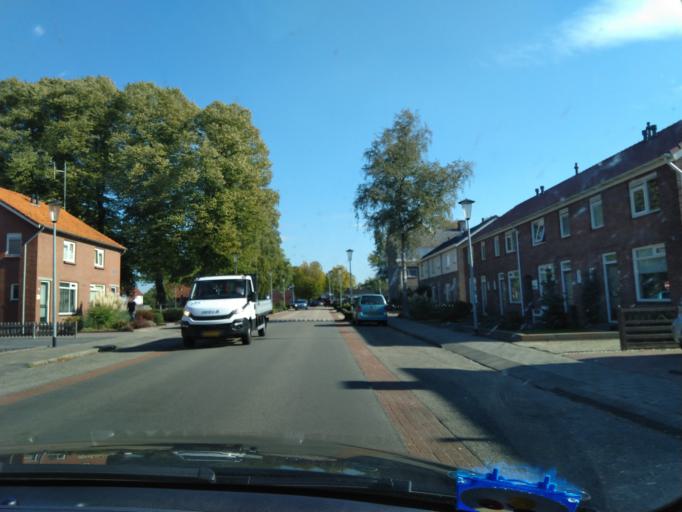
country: NL
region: Groningen
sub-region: Gemeente Veendam
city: Veendam
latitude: 53.0862
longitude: 6.8637
